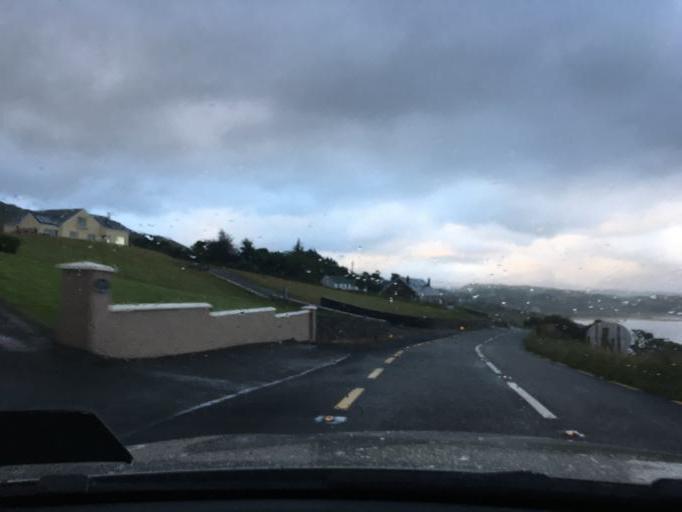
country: IE
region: Ulster
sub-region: County Donegal
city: Killybegs
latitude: 54.6302
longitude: -8.5107
